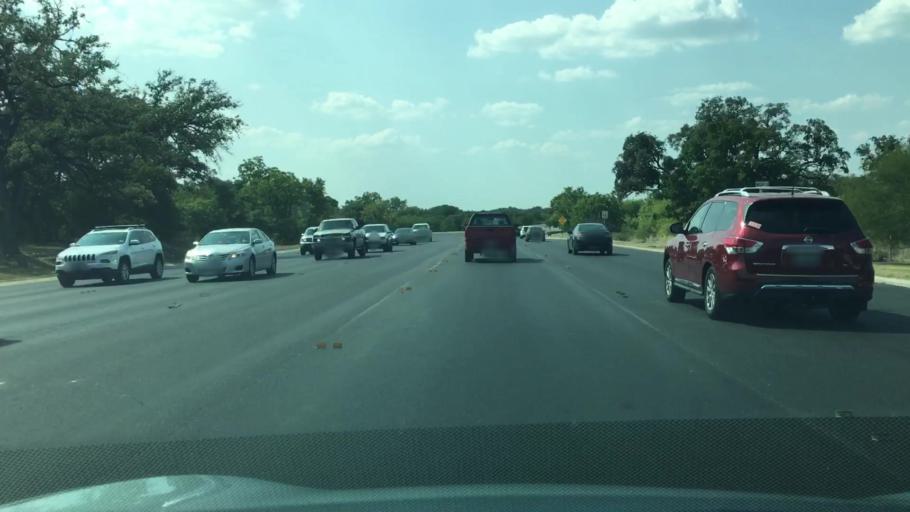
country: US
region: Texas
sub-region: Hays County
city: San Marcos
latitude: 29.8659
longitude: -97.9635
